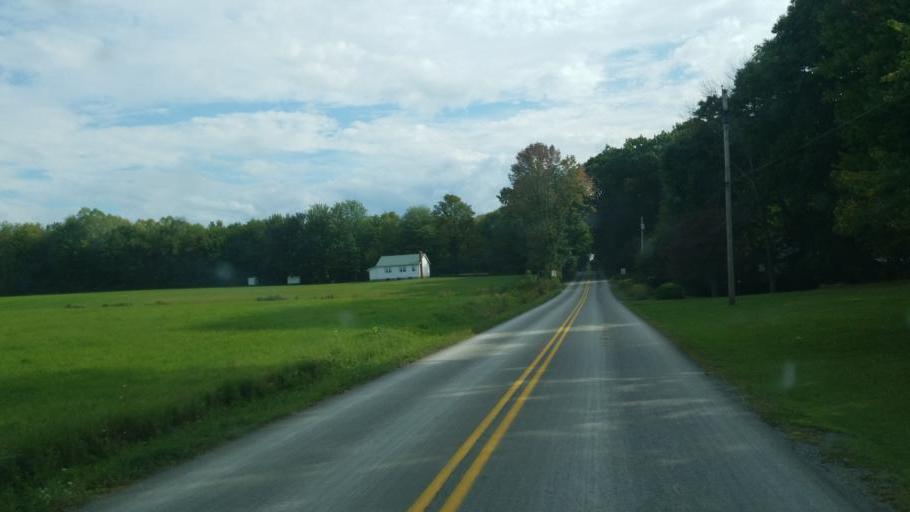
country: US
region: Pennsylvania
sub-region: Mercer County
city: Greenville
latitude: 41.4988
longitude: -80.3382
